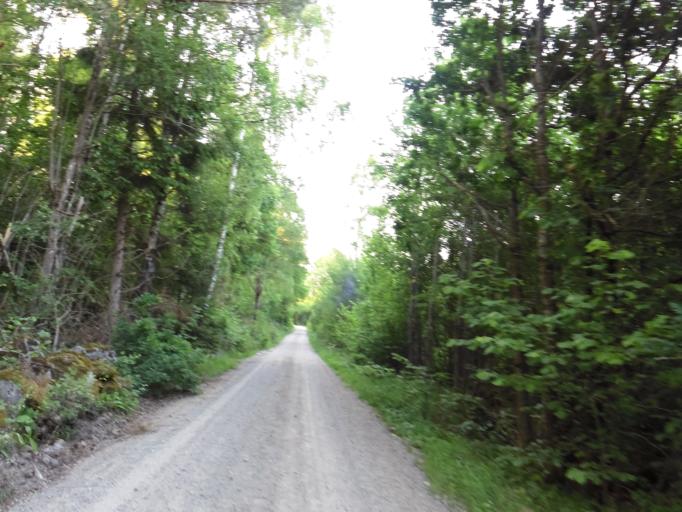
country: SE
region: Blekinge
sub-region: Olofstroms Kommun
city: Olofstroem
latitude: 56.4089
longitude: 14.5605
